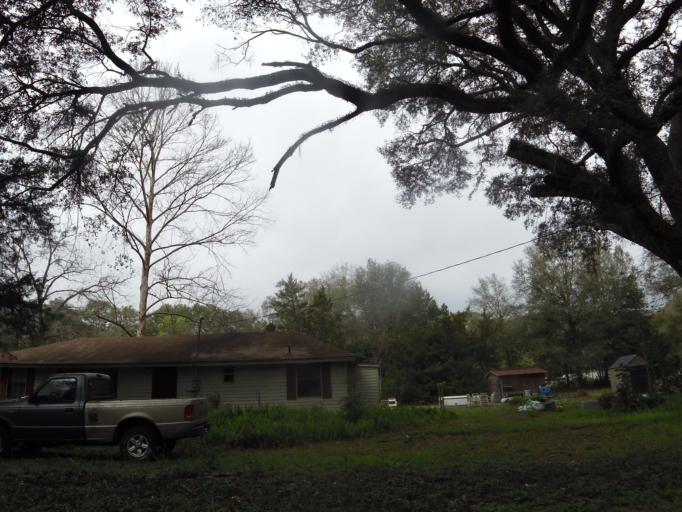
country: US
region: Florida
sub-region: Alachua County
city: High Springs
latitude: 29.8222
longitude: -82.6027
